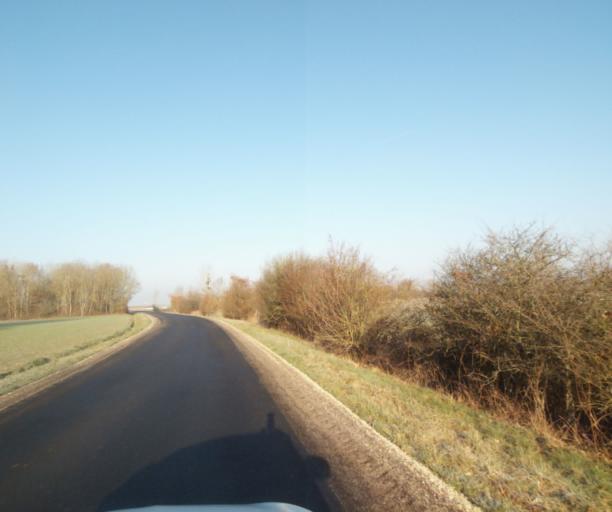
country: FR
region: Champagne-Ardenne
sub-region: Departement de la Haute-Marne
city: Montier-en-Der
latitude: 48.4906
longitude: 4.7351
